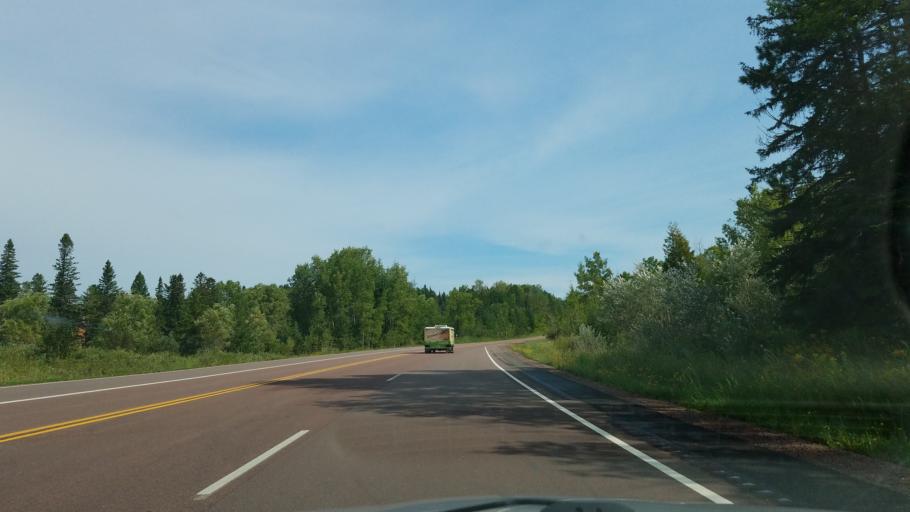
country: US
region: Wisconsin
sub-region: Ashland County
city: Ashland
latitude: 46.6017
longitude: -90.9542
